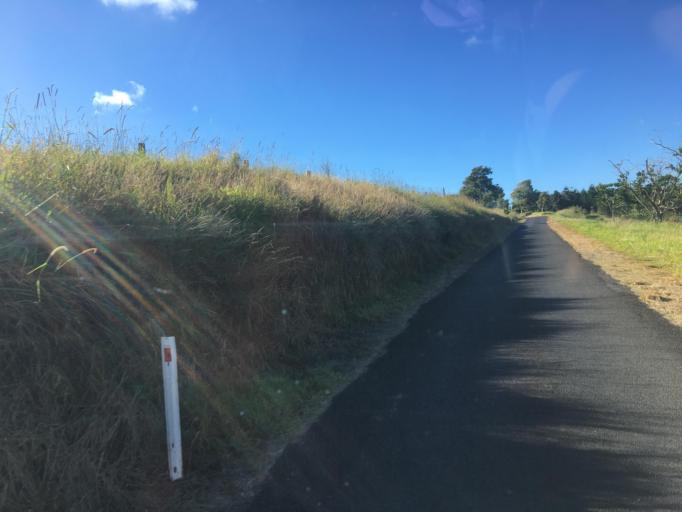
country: AU
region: Queensland
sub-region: Tablelands
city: Ravenshoe
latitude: -17.6021
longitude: 145.5332
